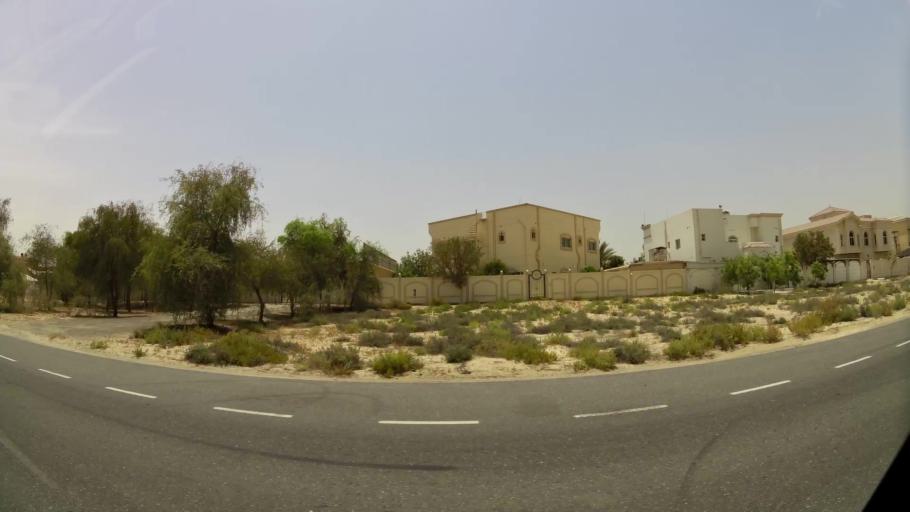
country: AE
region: Ash Shariqah
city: Sharjah
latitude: 25.1908
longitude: 55.3880
